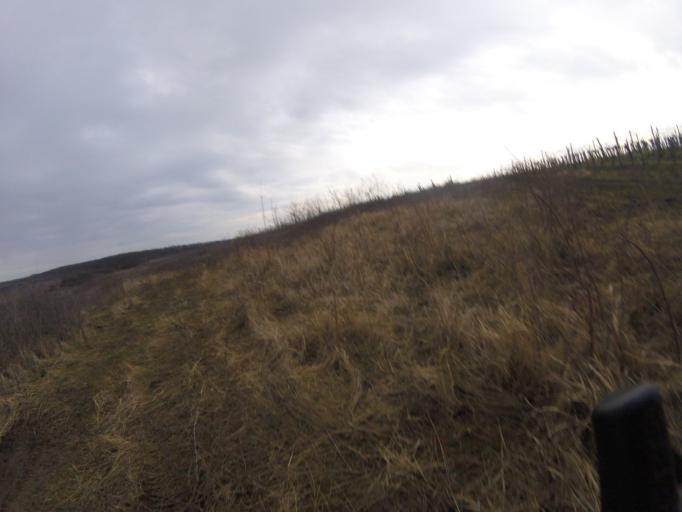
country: HU
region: Heves
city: Kerecsend
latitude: 47.8322
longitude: 20.3433
